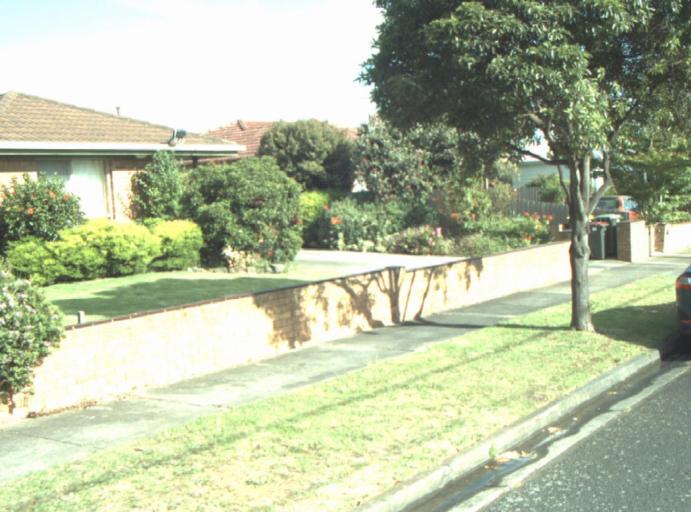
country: AU
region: Victoria
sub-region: Greater Geelong
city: Wandana Heights
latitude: -38.1770
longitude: 144.3327
